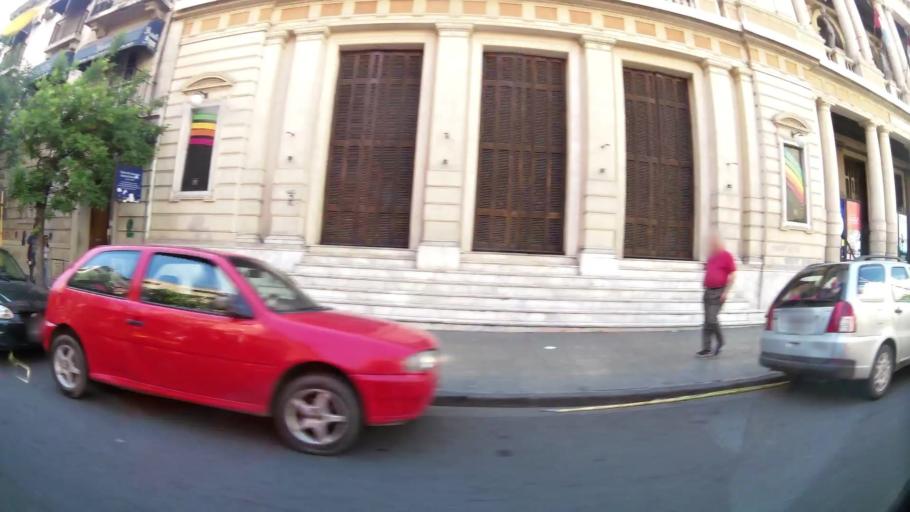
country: AR
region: Cordoba
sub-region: Departamento de Capital
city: Cordoba
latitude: -31.4191
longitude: -64.1883
